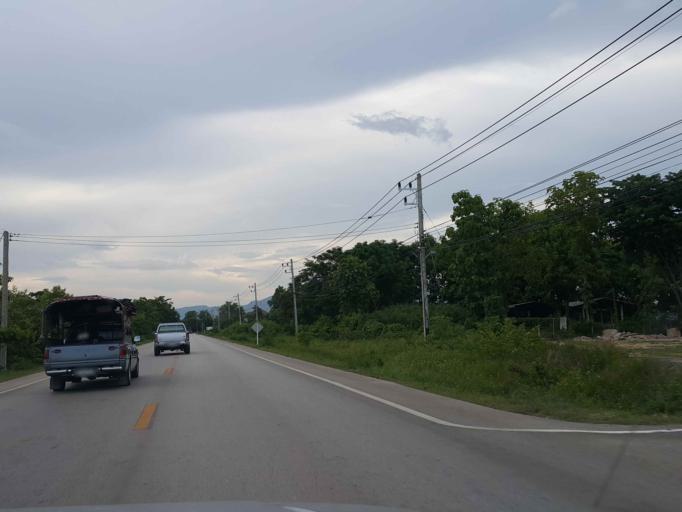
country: TH
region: Lampang
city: Hang Chat
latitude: 18.3008
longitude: 99.3711
